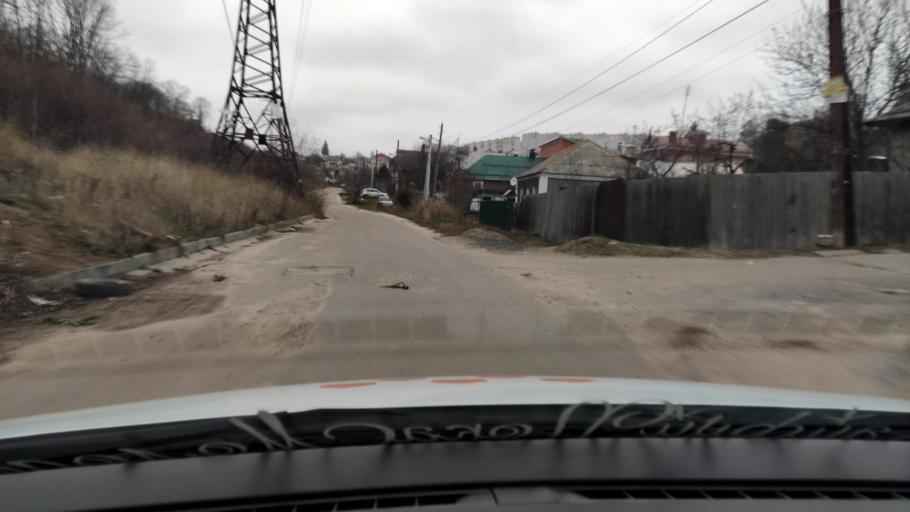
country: RU
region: Voronezj
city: Voronezh
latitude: 51.6266
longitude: 39.1890
